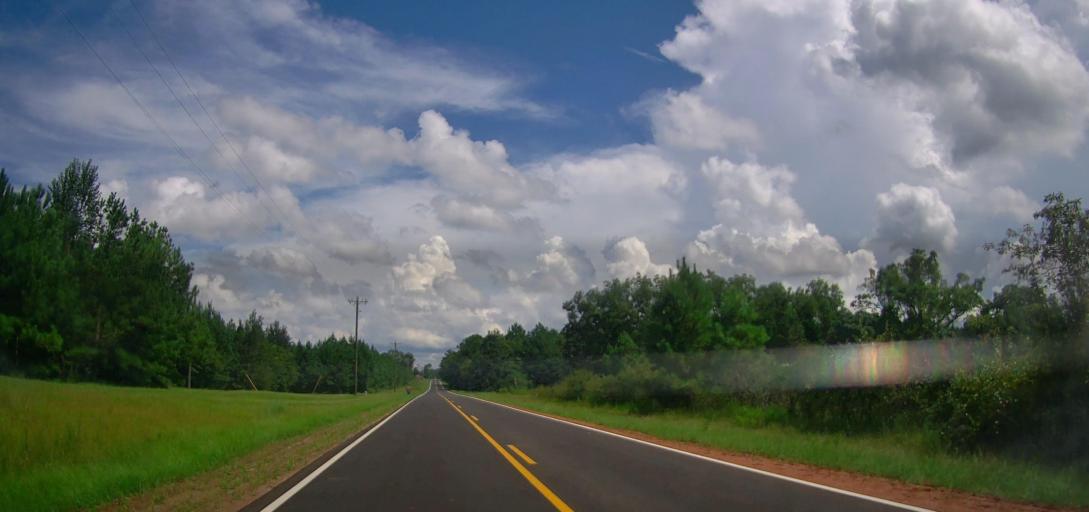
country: US
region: Georgia
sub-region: Macon County
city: Marshallville
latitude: 32.4725
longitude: -83.8736
